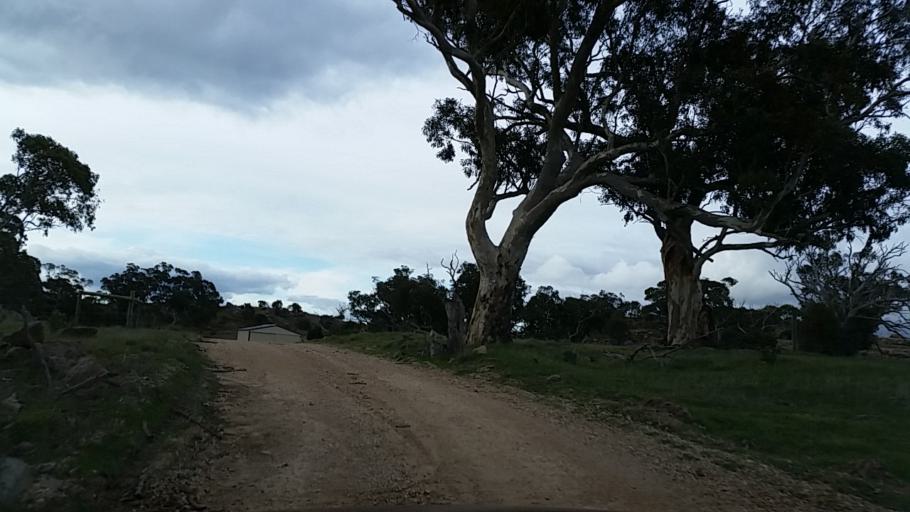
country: AU
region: South Australia
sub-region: Mount Barker
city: Callington
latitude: -34.9565
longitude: 139.0575
